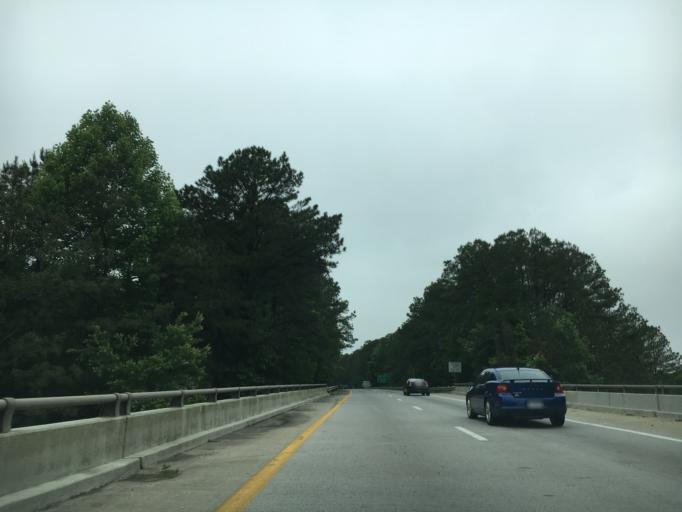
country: US
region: Virginia
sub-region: Chesterfield County
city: Matoaca
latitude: 37.1959
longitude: -77.4809
